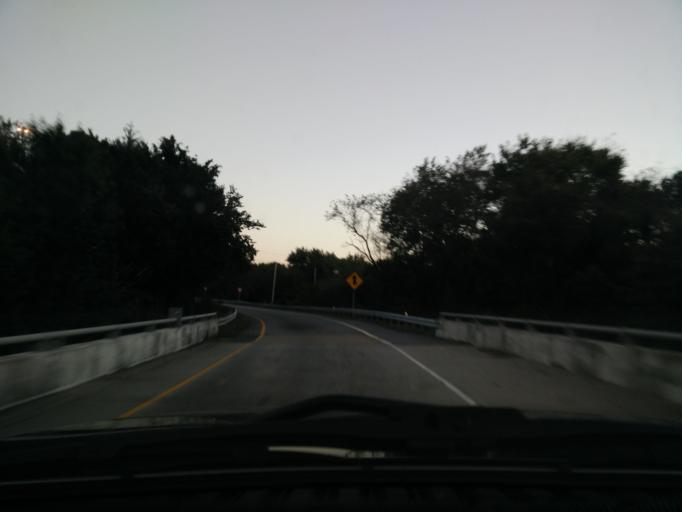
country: US
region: Virginia
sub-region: City of Chesapeake
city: Chesapeake
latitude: 36.8442
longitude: -76.1987
